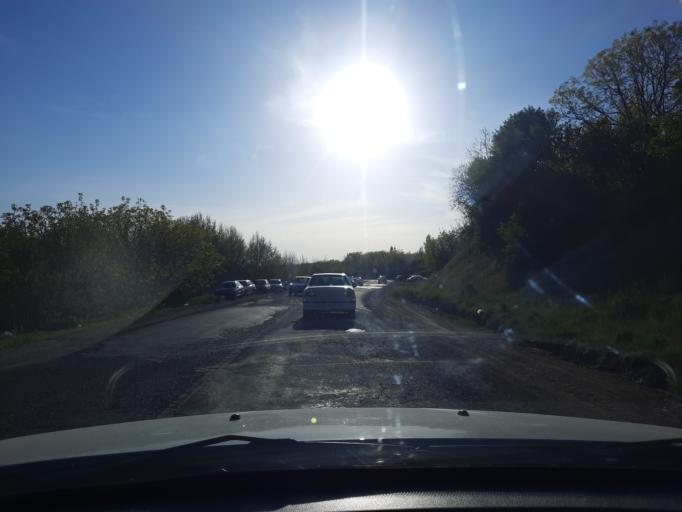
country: IR
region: Qazvin
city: Qazvin
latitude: 36.3409
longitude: 50.1684
